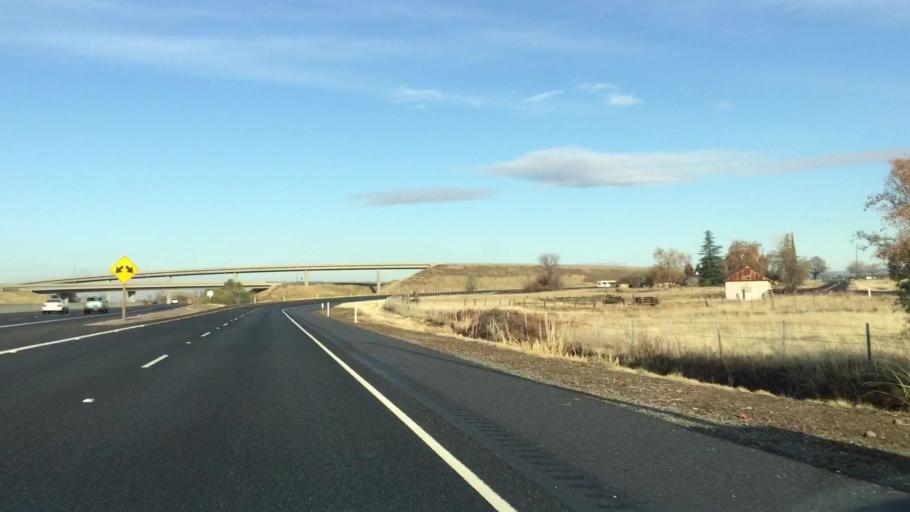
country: US
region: California
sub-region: Butte County
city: Thermalito
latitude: 39.5792
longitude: -121.6196
